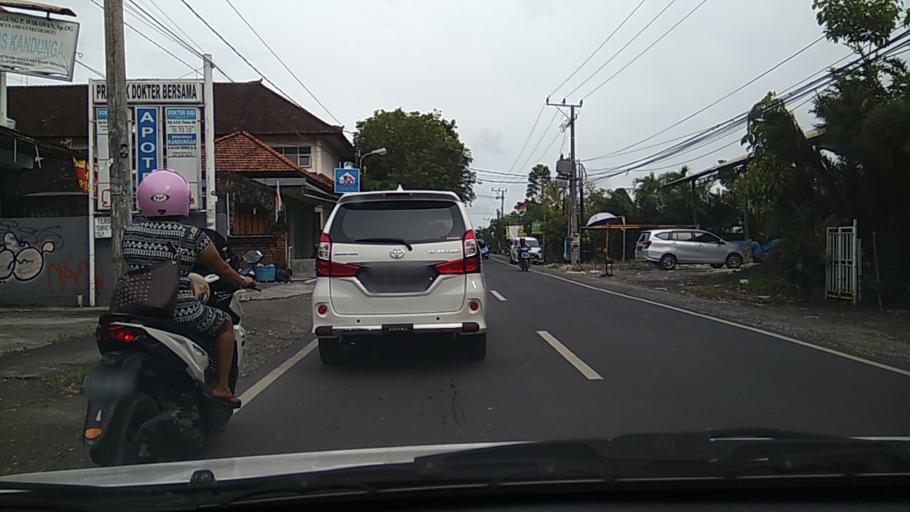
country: ID
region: Bali
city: Banjar Gunungpande
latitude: -8.6405
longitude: 115.1526
